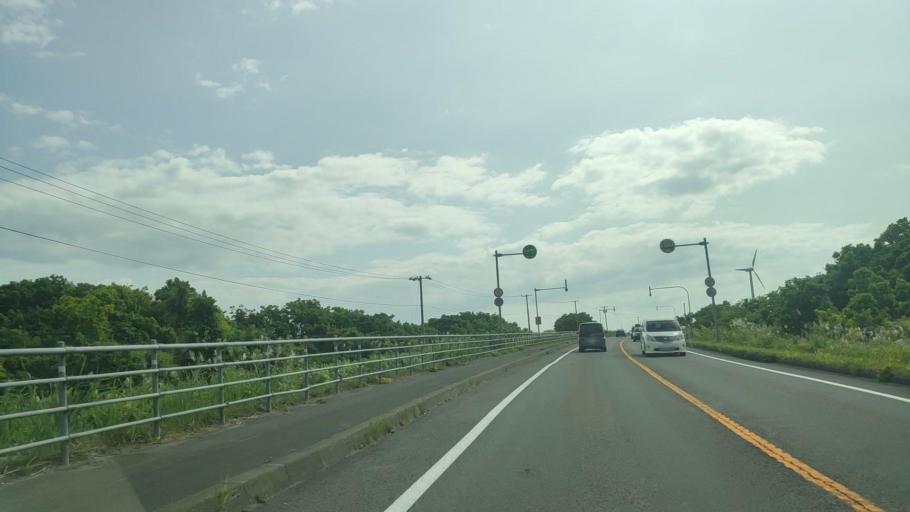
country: JP
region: Hokkaido
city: Rumoi
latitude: 44.3286
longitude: 141.6776
